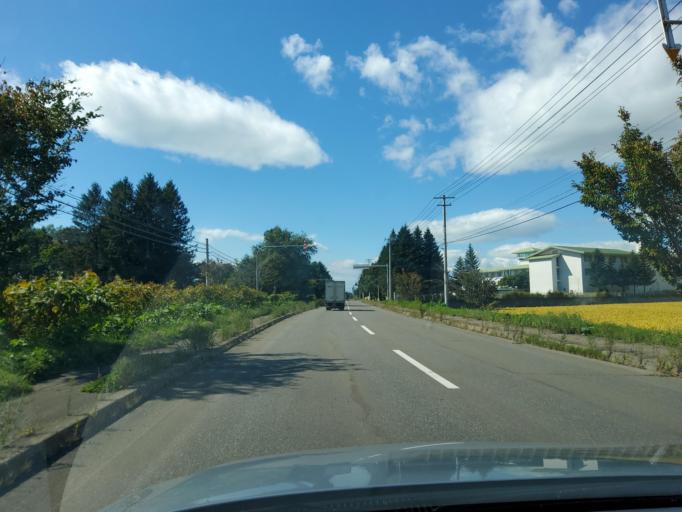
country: JP
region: Hokkaido
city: Obihiro
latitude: 42.9362
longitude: 143.2908
